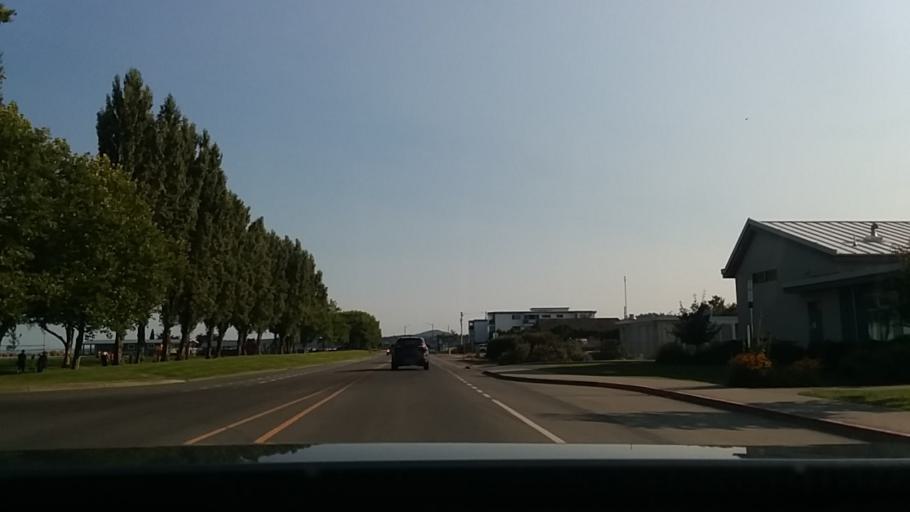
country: CA
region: British Columbia
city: North Saanich
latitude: 48.6438
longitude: -123.4004
